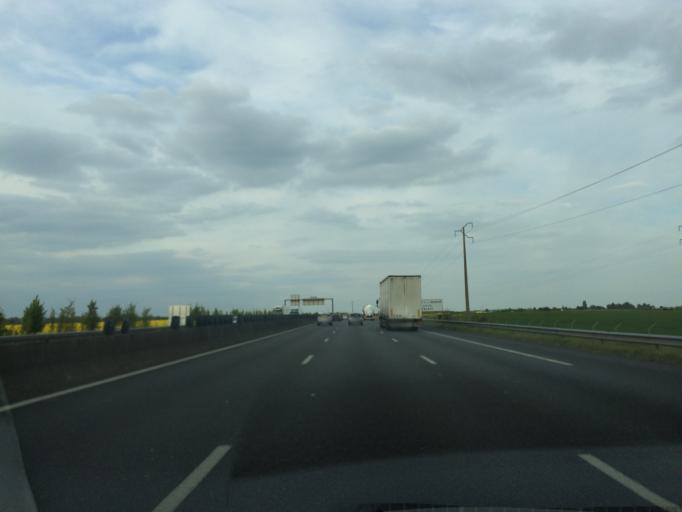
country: FR
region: Picardie
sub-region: Departement de l'Oise
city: Chamant
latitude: 49.2221
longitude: 2.6406
